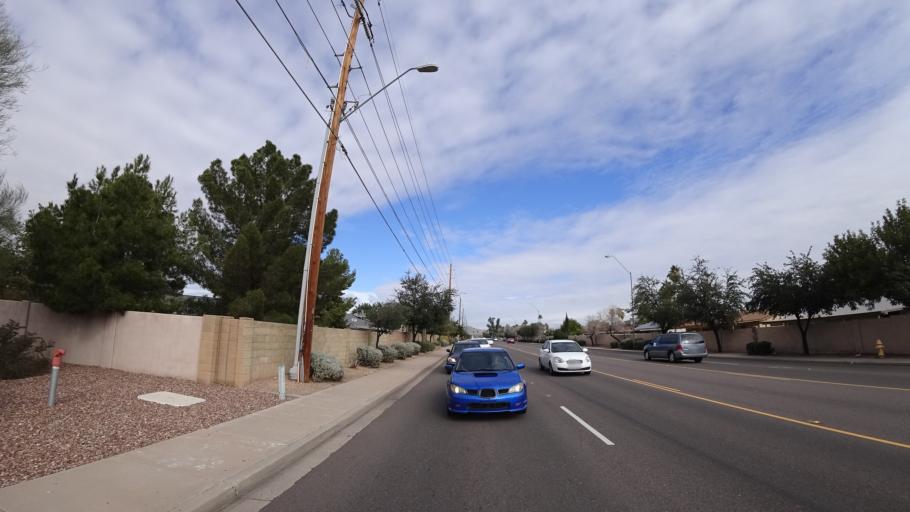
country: US
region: Arizona
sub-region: Maricopa County
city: Peoria
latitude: 33.6447
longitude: -112.1865
